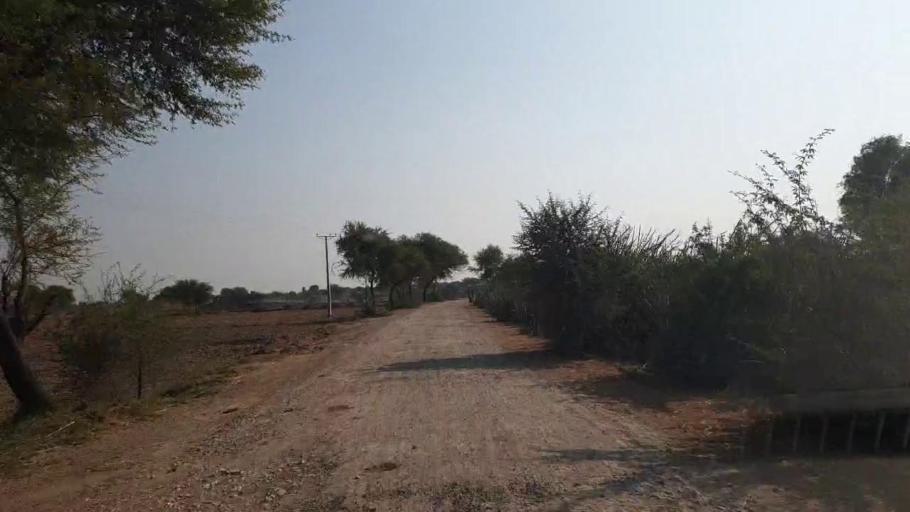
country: PK
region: Sindh
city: Kario
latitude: 24.9165
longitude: 68.6519
